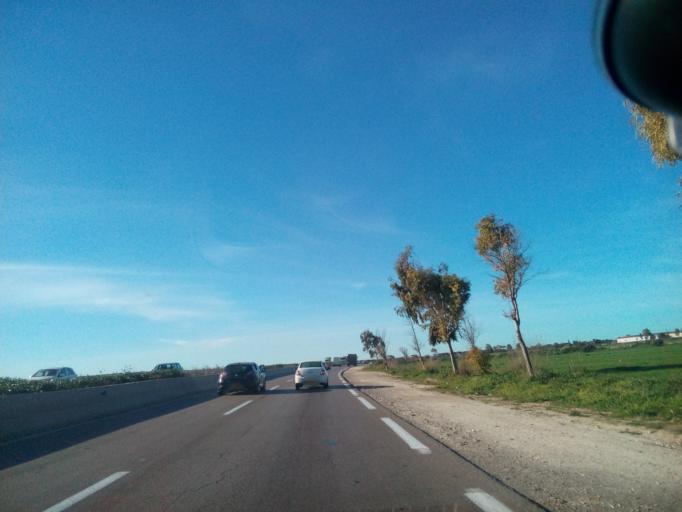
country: DZ
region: Oran
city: Ain el Bya
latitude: 35.7689
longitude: -0.2027
